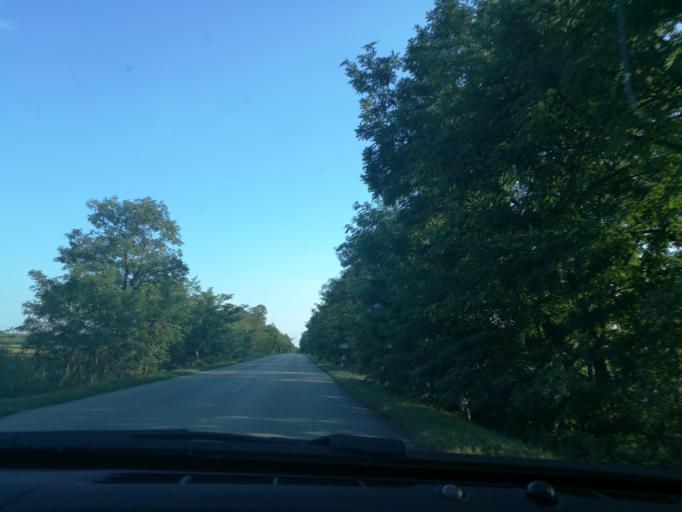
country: HU
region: Szabolcs-Szatmar-Bereg
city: Tiszabercel
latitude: 48.1322
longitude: 21.6463
